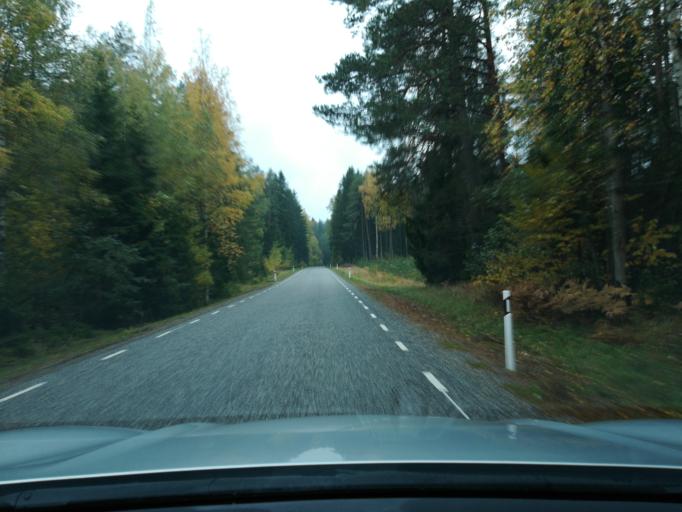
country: EE
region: Ida-Virumaa
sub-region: Johvi vald
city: Johvi
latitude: 59.1575
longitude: 27.4047
